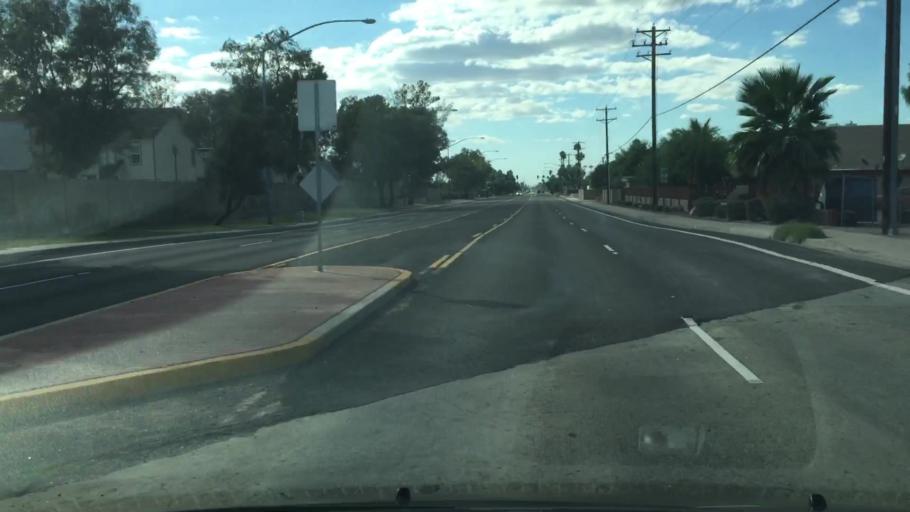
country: US
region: Arizona
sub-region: Maricopa County
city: Mesa
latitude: 33.4082
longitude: -111.7764
